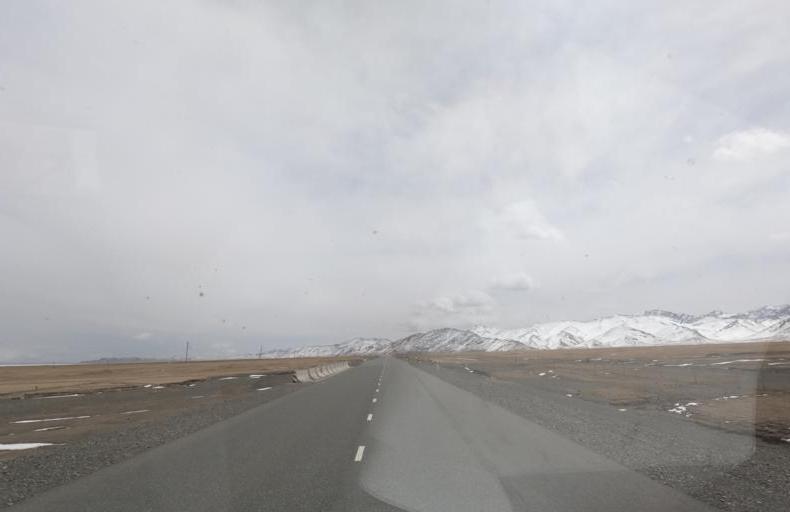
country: KG
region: Naryn
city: Baetov
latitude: 40.5523
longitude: 75.2171
